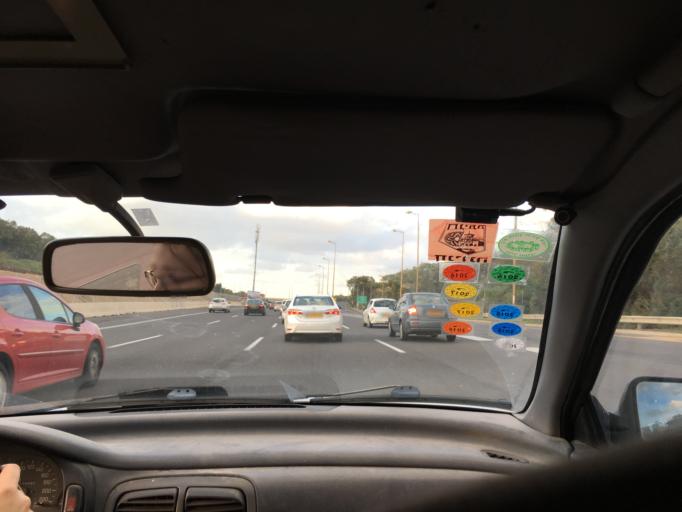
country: IL
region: Tel Aviv
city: Ramat Gan
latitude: 32.1147
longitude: 34.8111
